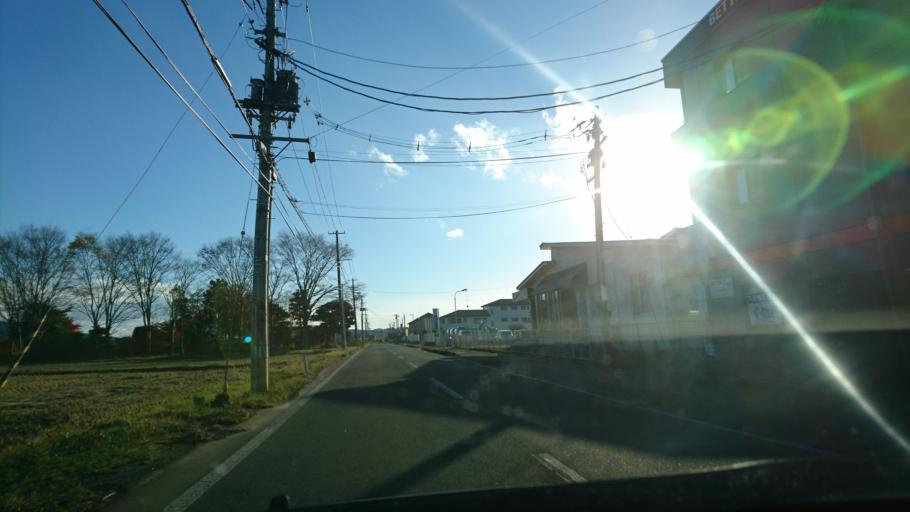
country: JP
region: Iwate
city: Mizusawa
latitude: 39.0511
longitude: 141.1363
